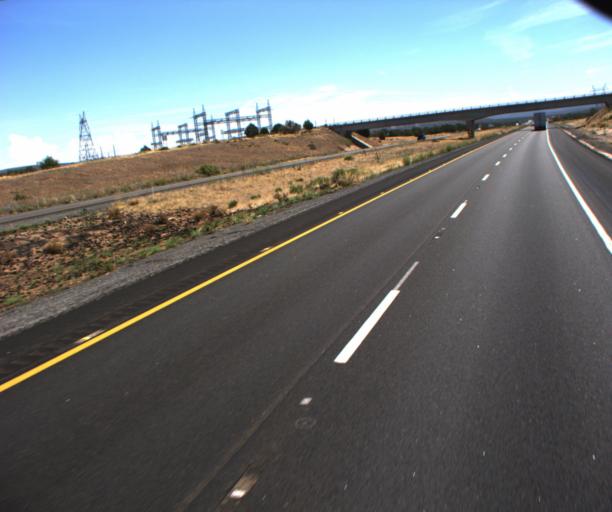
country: US
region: Arizona
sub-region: Mohave County
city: Peach Springs
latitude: 35.1906
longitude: -113.3672
